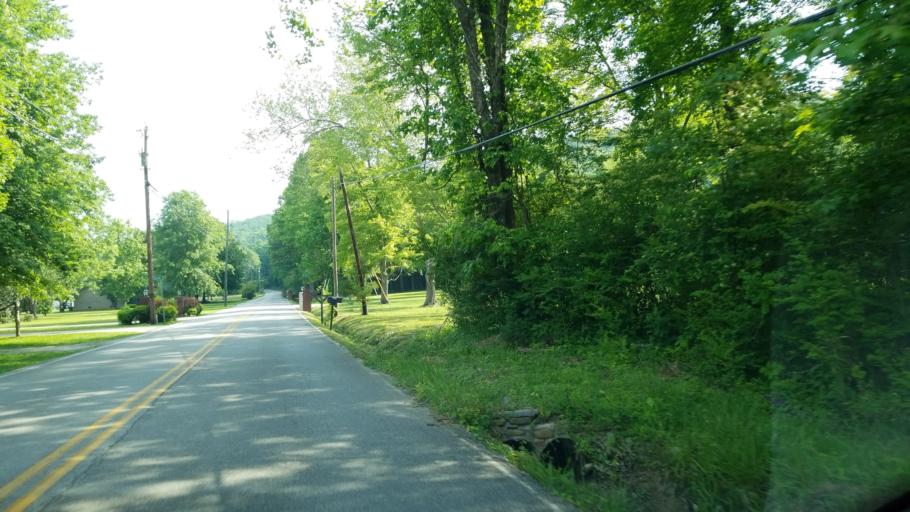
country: US
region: Tennessee
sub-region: Hamilton County
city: Collegedale
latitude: 35.0925
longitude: -85.0147
